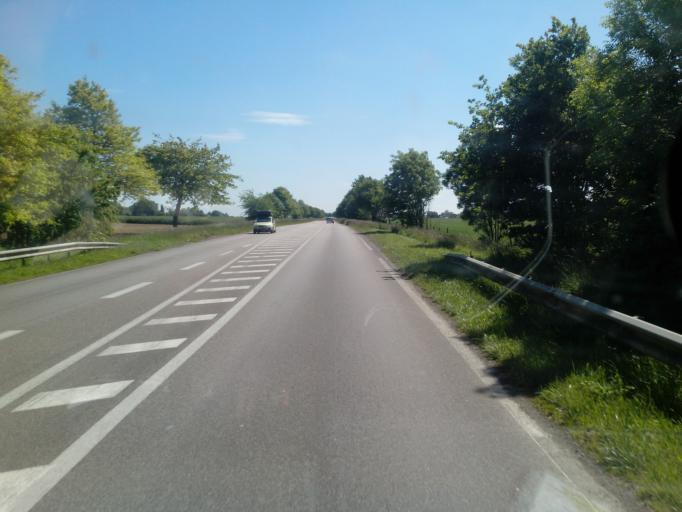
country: FR
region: Haute-Normandie
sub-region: Departement de l'Eure
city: Beuzeville
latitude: 49.3782
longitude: 0.3995
